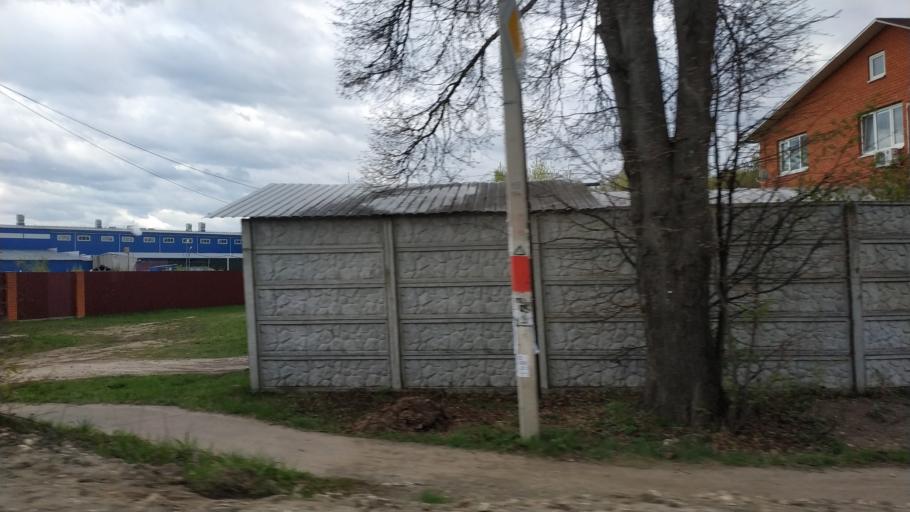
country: RU
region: Moskovskaya
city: Pavlovskiy Posad
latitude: 55.7717
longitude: 38.6912
